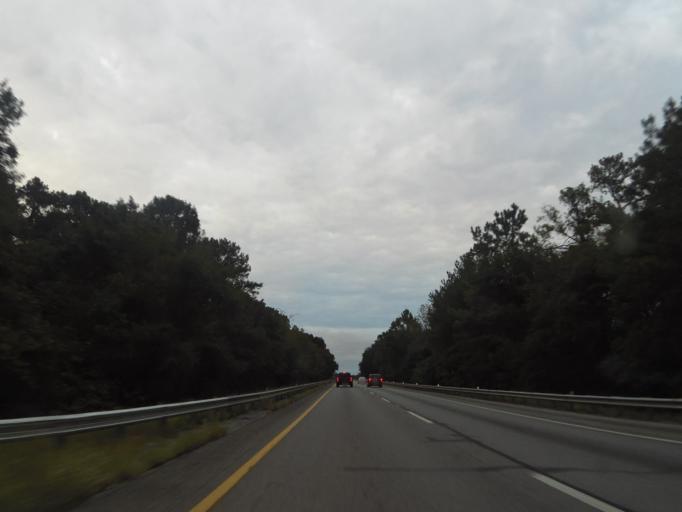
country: US
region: Alabama
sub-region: Saint Clair County
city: Ashville
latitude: 33.8808
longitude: -86.2595
